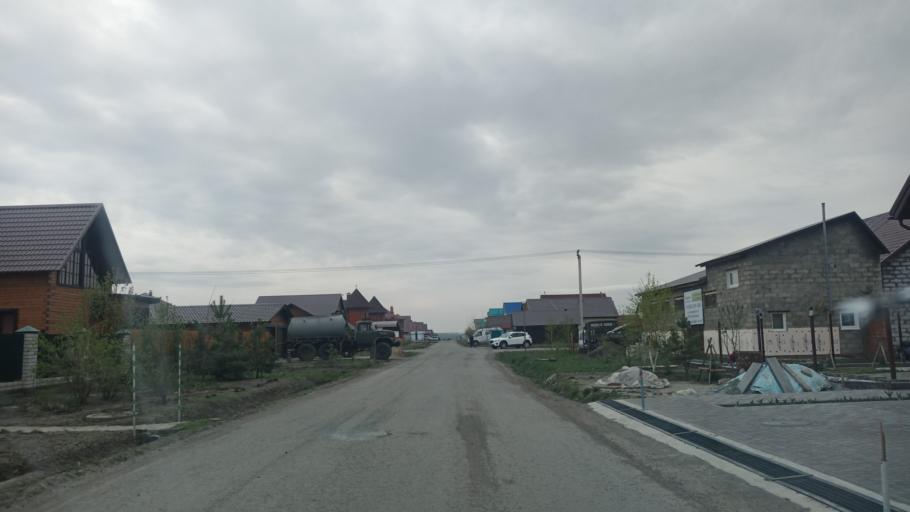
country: RU
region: Altai Krai
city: Yuzhnyy
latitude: 53.2235
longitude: 83.6904
